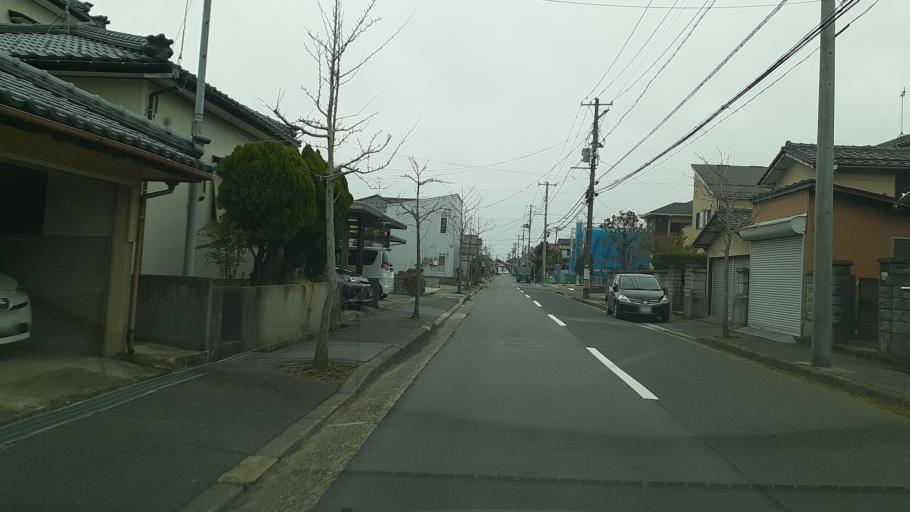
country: JP
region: Niigata
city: Niigata-shi
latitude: 37.8623
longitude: 139.0398
